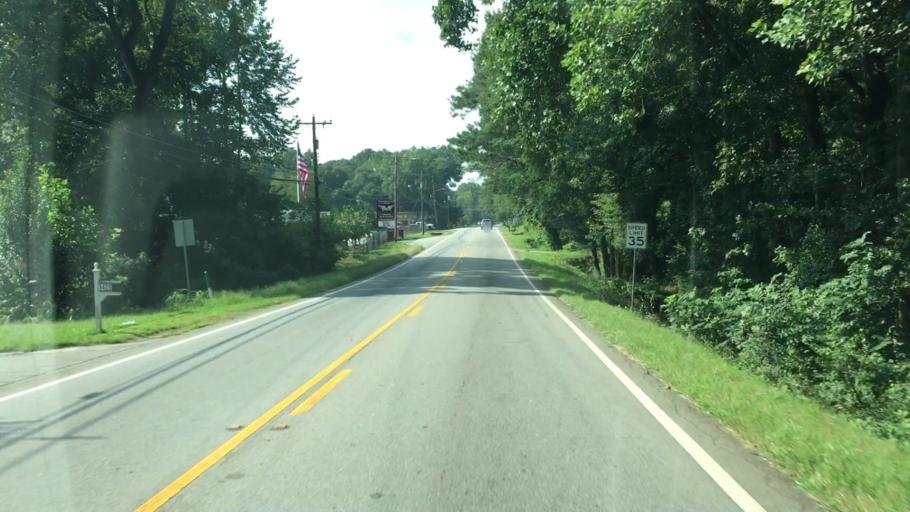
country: US
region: Georgia
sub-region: Walton County
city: Monroe
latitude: 33.7770
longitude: -83.7051
